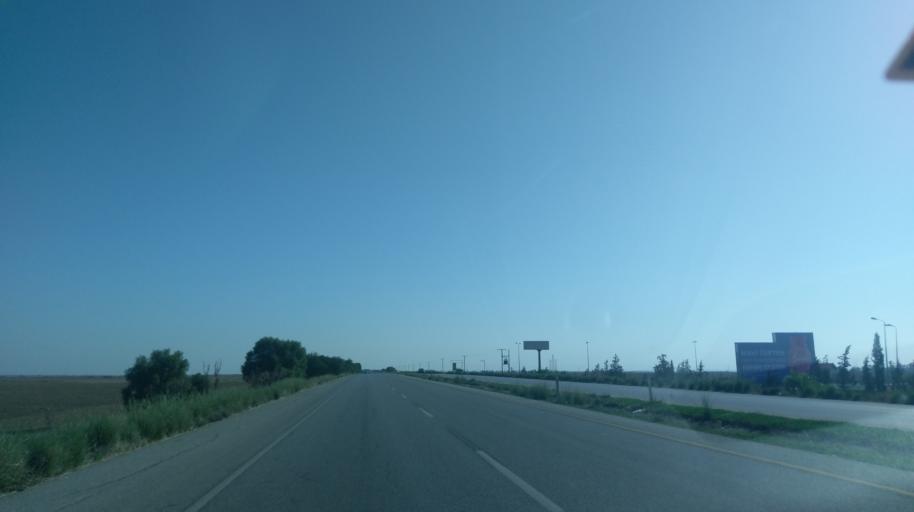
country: CY
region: Ammochostos
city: Lefkonoiko
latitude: 35.1843
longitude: 33.6823
